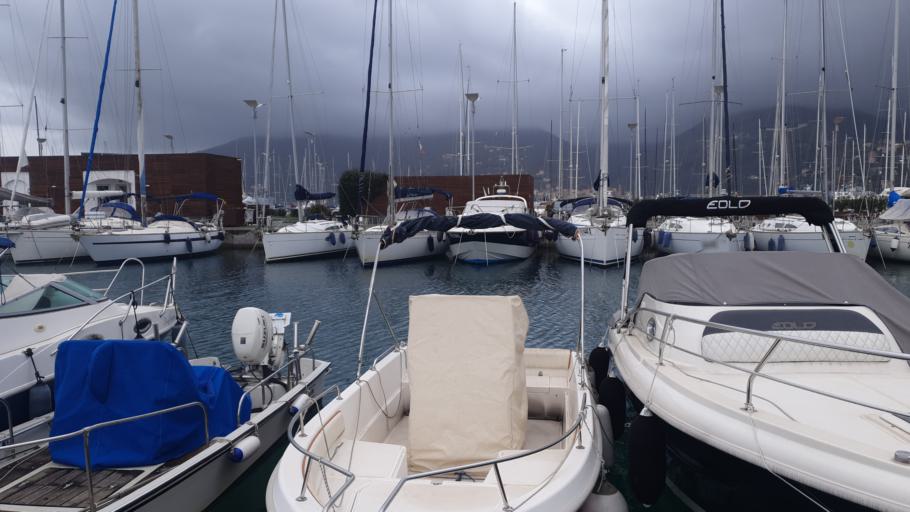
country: IT
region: Liguria
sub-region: Provincia di La Spezia
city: La Spezia
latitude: 44.1000
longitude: 9.8312
